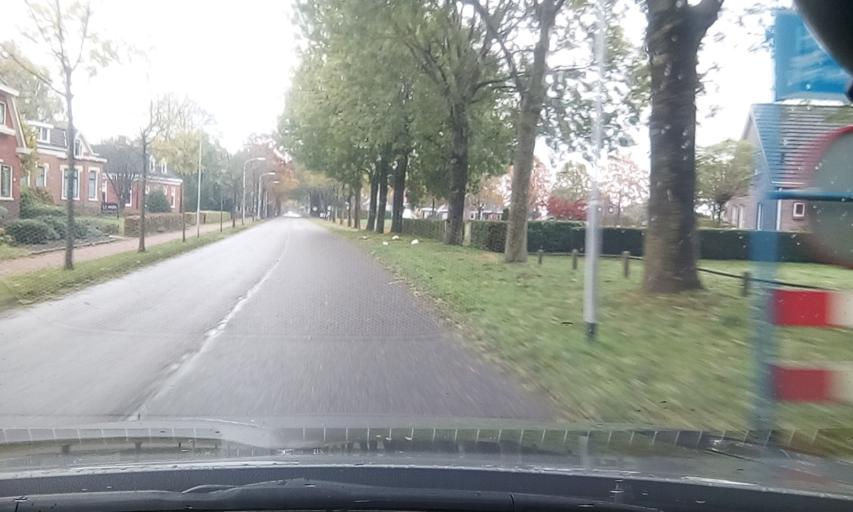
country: NL
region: Groningen
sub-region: Gemeente Haren
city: Haren
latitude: 53.2093
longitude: 6.6800
